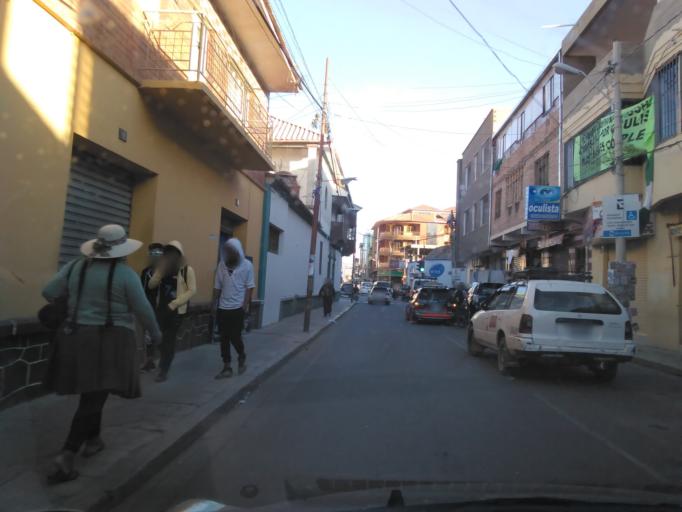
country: BO
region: Cochabamba
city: Punata
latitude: -17.5446
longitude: -65.8368
